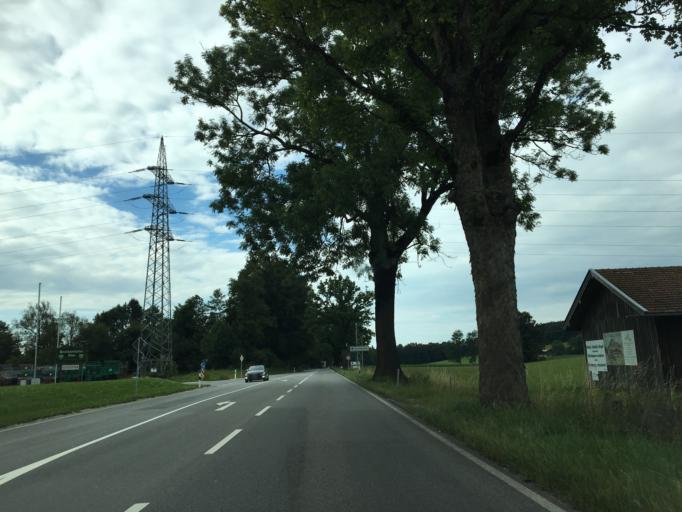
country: DE
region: Bavaria
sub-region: Upper Bavaria
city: Warngau
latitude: 47.7938
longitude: 11.7204
